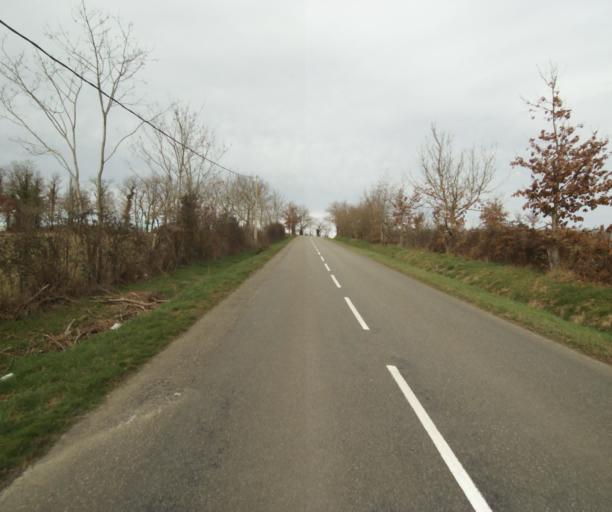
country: FR
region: Aquitaine
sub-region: Departement des Landes
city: Gabarret
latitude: 43.9625
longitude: 0.0050
